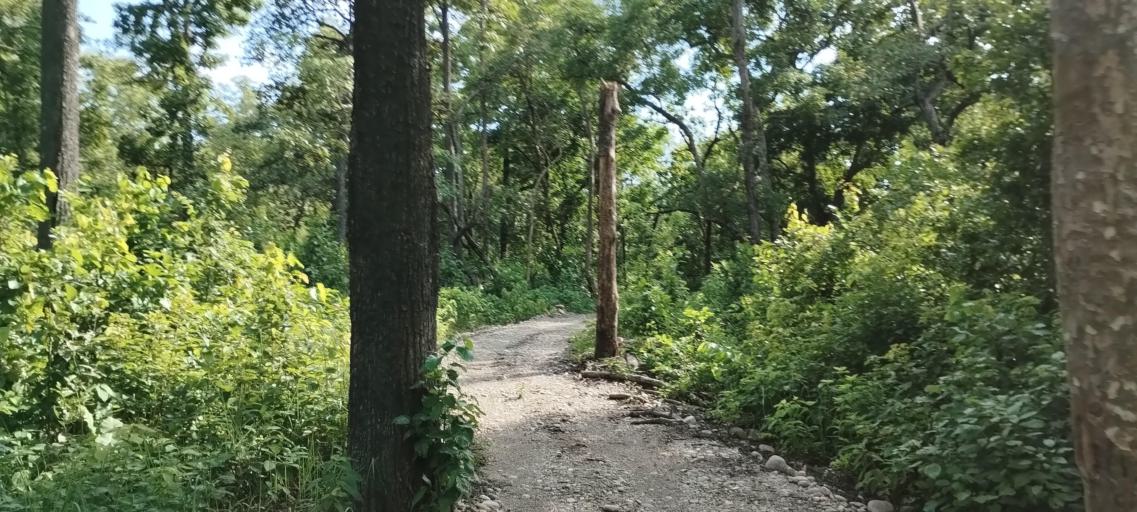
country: NP
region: Far Western
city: Tikapur
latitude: 28.5616
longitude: 81.2664
